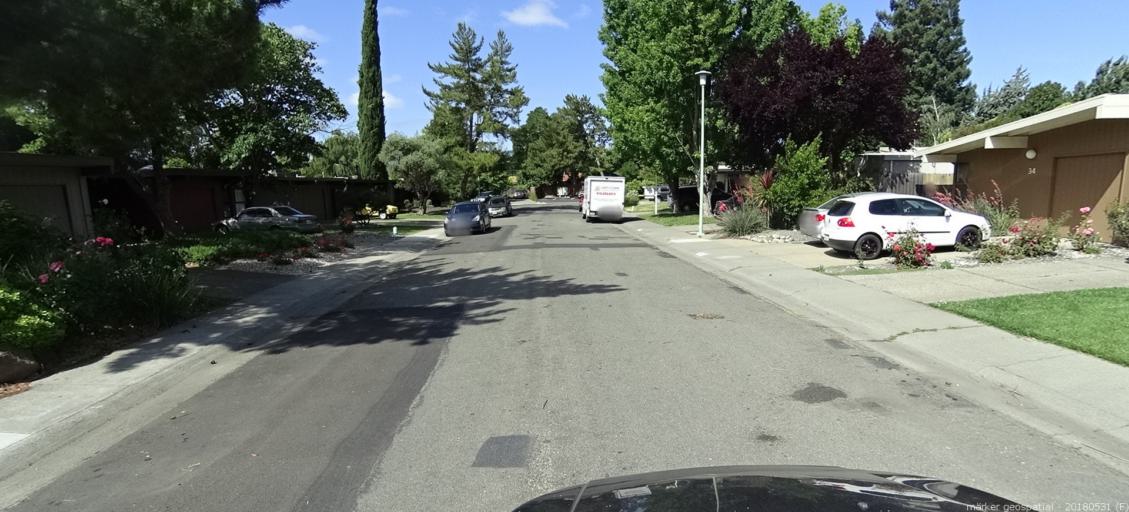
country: US
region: California
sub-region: Sacramento County
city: Sacramento
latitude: 38.6163
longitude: -121.5012
